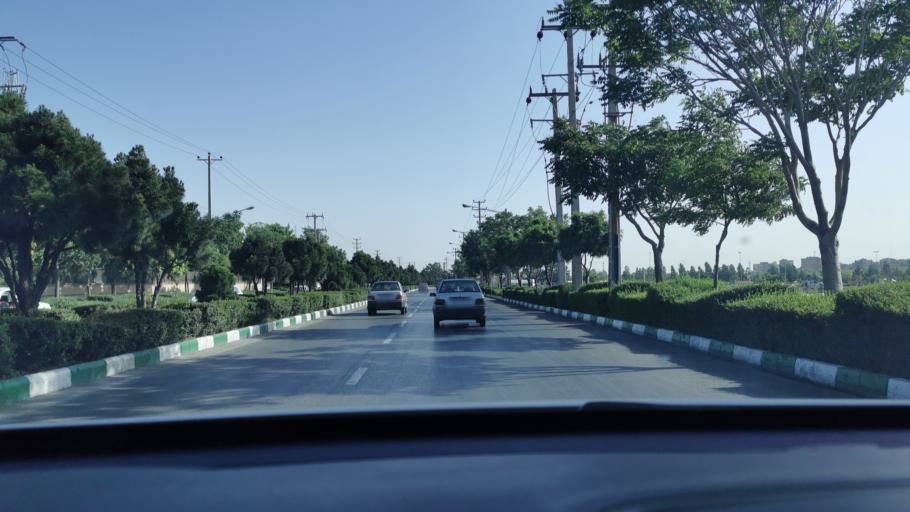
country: IR
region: Razavi Khorasan
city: Mashhad
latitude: 36.3426
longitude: 59.5080
